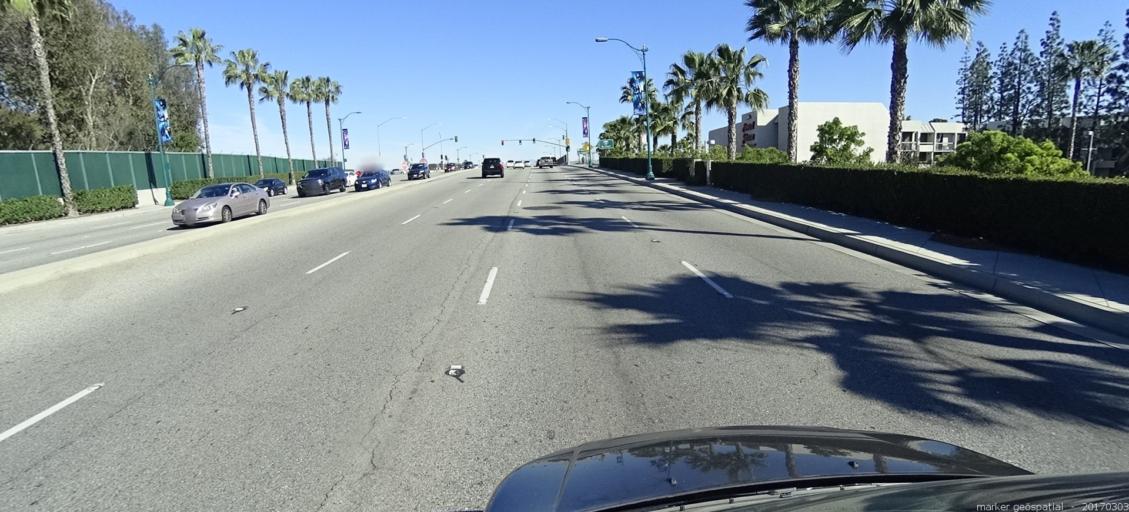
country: US
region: California
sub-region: Orange County
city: Anaheim
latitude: 33.8132
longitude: -117.9153
